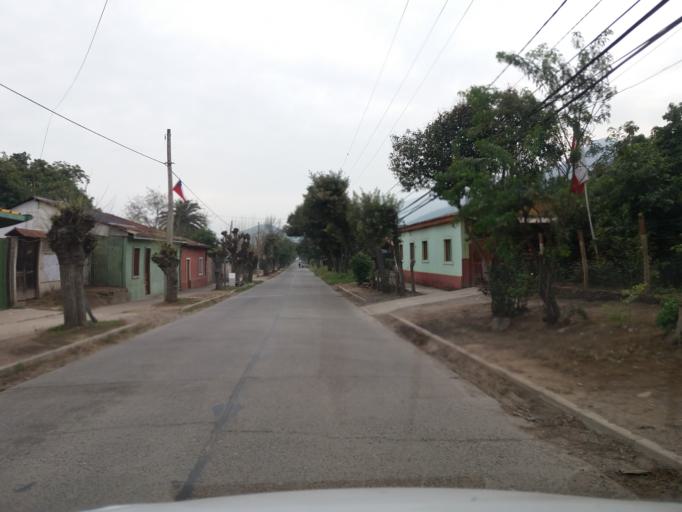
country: CL
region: Valparaiso
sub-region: Provincia de Quillota
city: Hacienda La Calera
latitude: -32.8102
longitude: -71.1413
